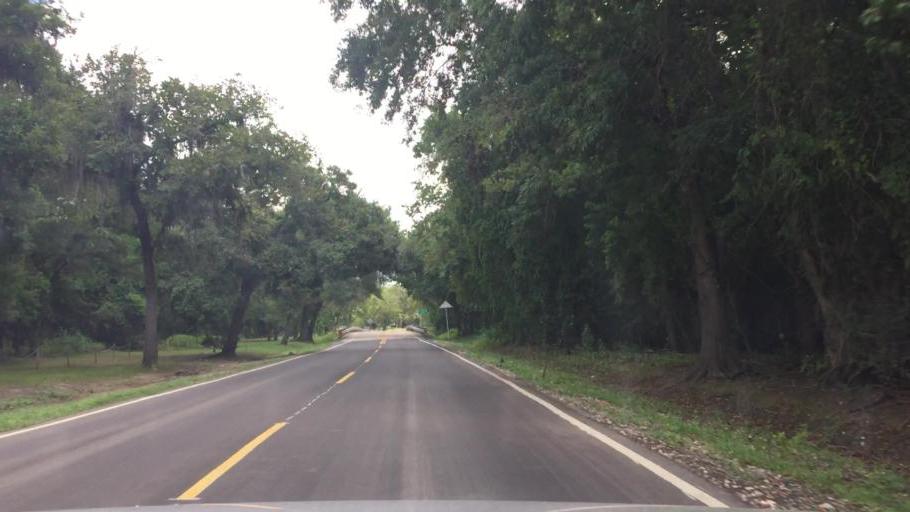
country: US
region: Texas
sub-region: Harris County
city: Jersey Village
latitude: 29.8134
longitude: -95.6304
